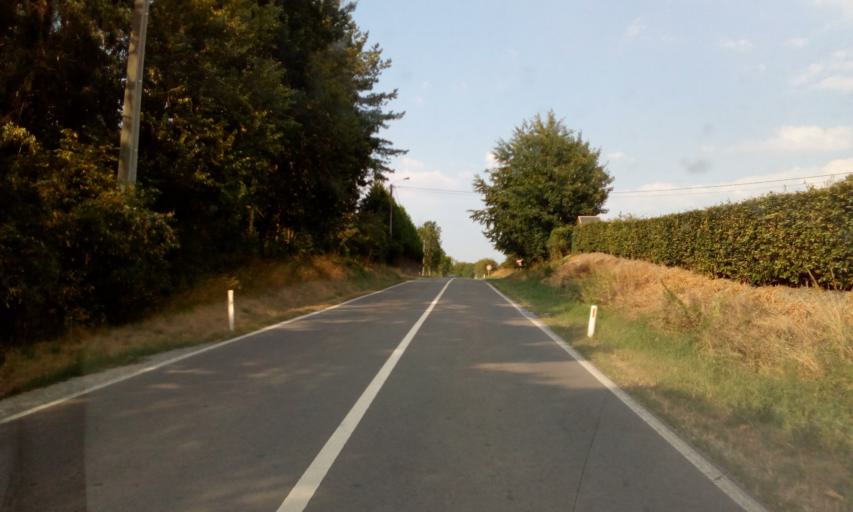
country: BE
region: Wallonia
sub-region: Province du Luxembourg
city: Tellin
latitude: 50.1137
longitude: 5.2426
